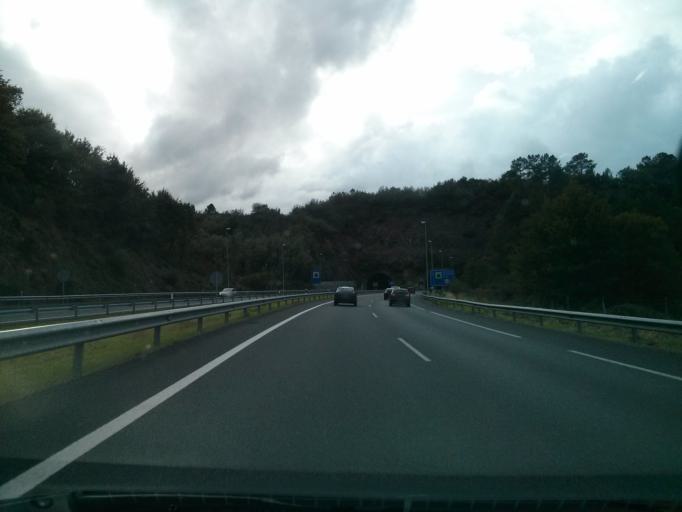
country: ES
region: Galicia
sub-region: Provincia de Ourense
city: Toen
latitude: 42.3306
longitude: -7.9521
